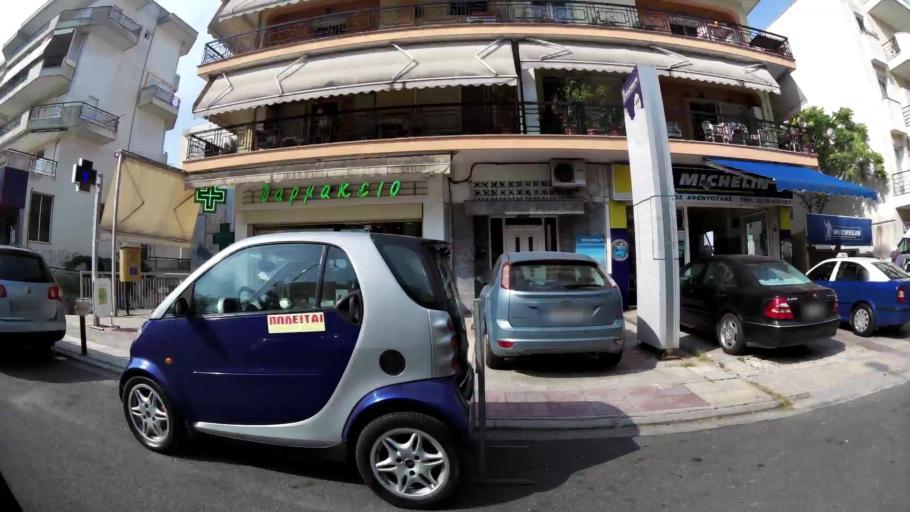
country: GR
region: Central Macedonia
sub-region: Nomos Thessalonikis
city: Sykies
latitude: 40.6521
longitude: 22.9561
